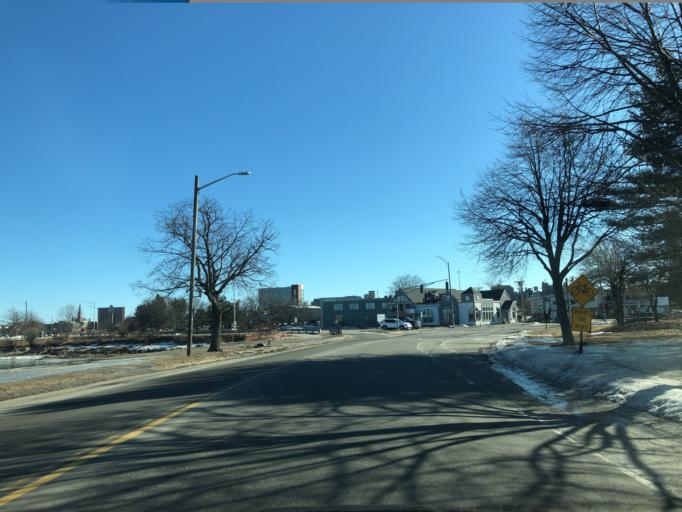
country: US
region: Maine
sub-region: Cumberland County
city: Portland
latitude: 43.6658
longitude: -70.2715
